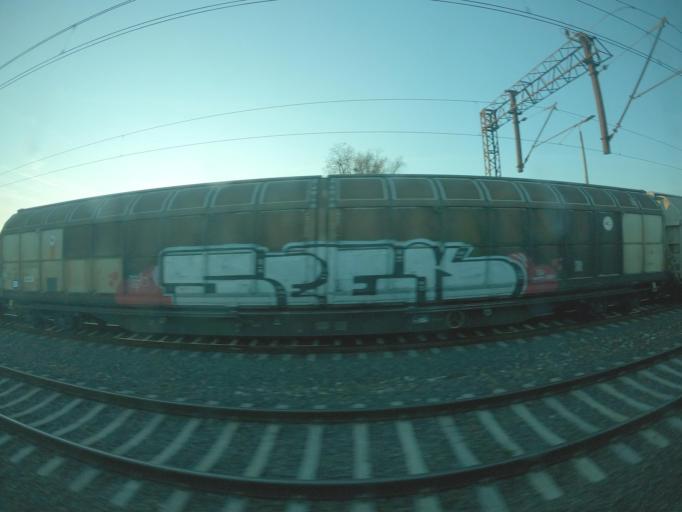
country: PL
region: Lubusz
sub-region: Powiat slubicki
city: Gorzyca
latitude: 52.5201
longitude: 14.6507
